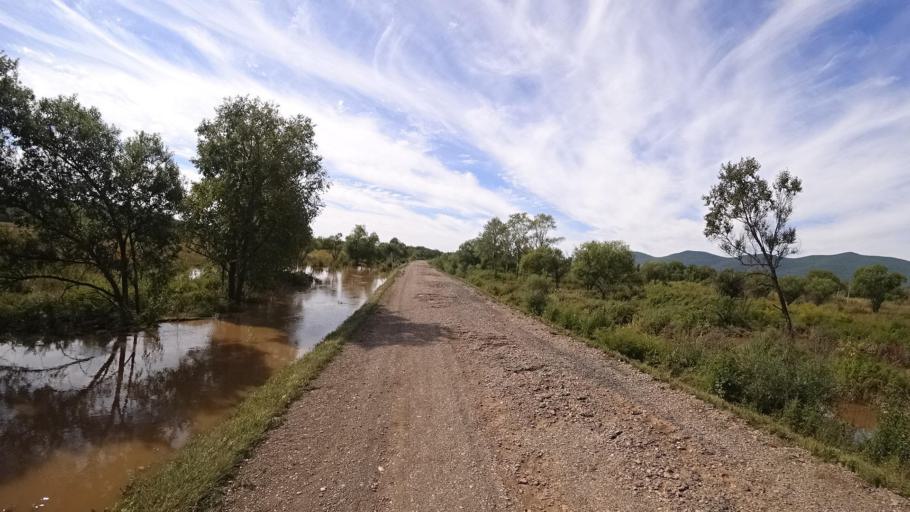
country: RU
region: Primorskiy
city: Kirovskiy
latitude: 44.7692
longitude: 133.6222
